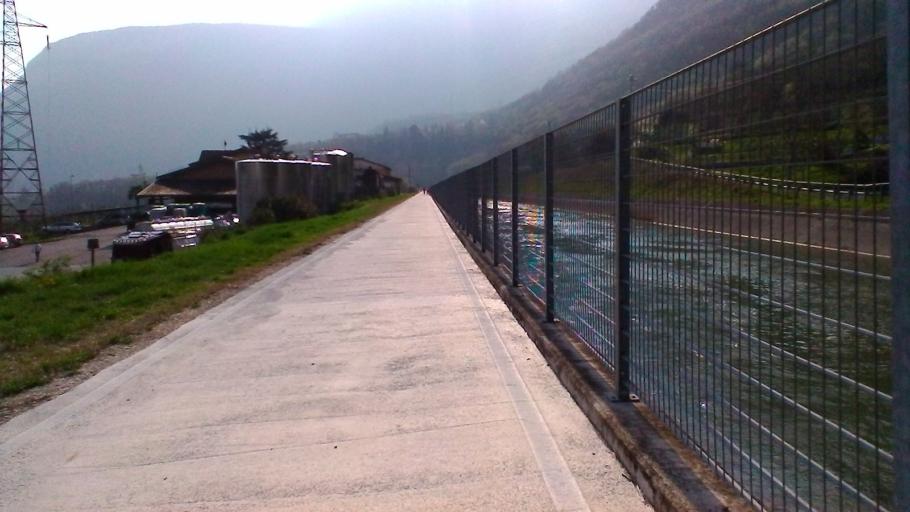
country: IT
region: Veneto
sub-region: Provincia di Verona
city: Rivalta
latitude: 45.6927
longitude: 10.9065
